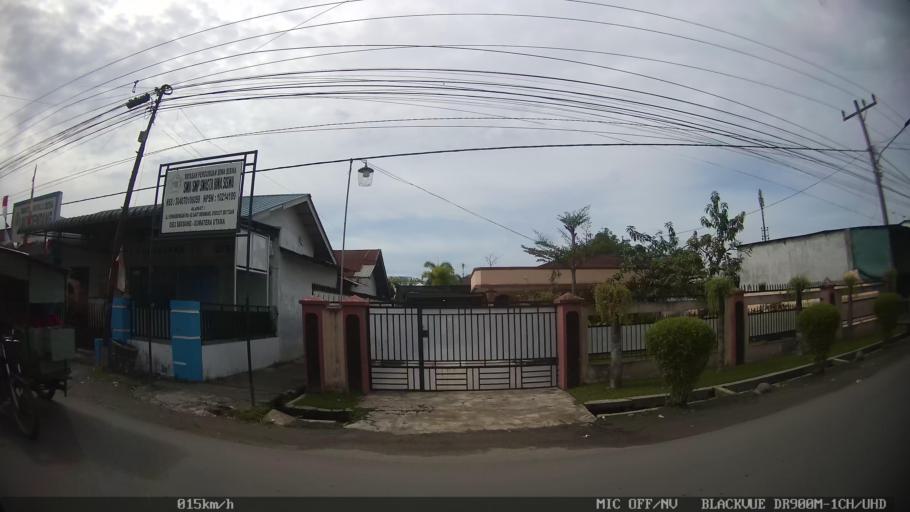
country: ID
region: North Sumatra
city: Medan
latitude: 3.6207
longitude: 98.7264
